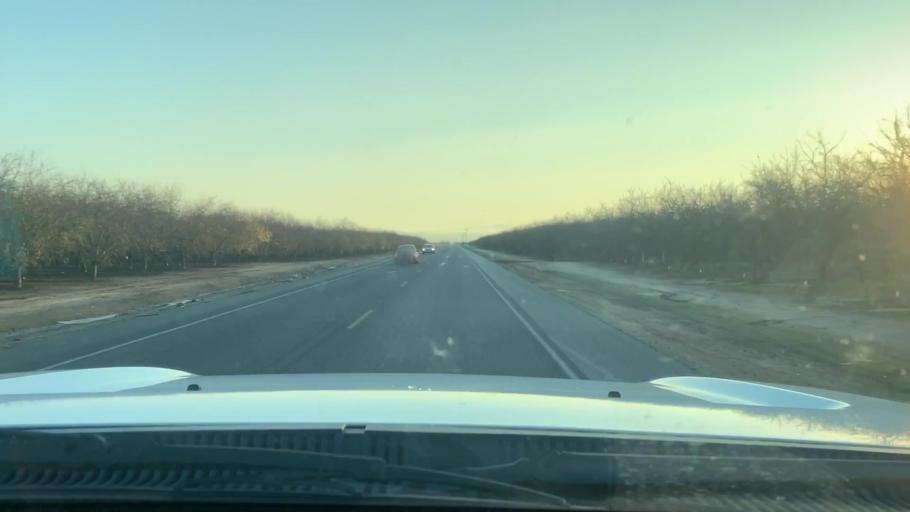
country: US
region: California
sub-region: Kern County
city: Wasco
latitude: 35.5002
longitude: -119.3953
